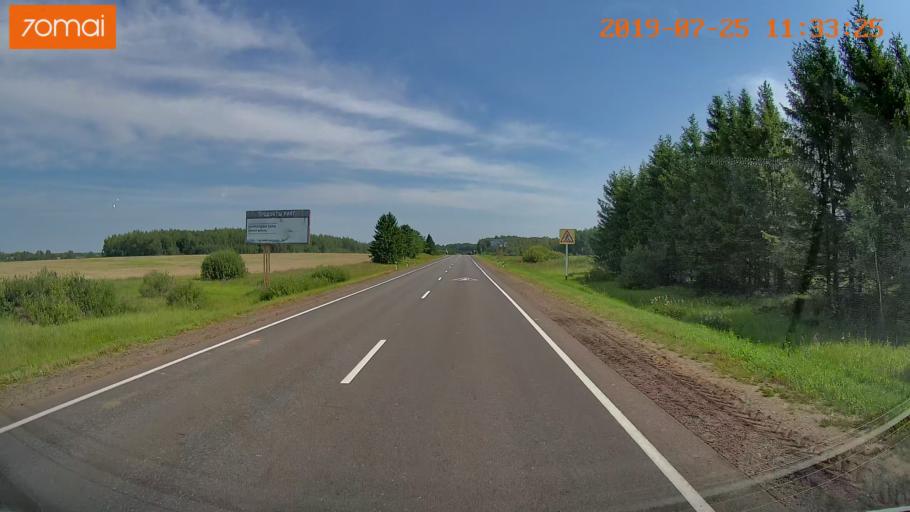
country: RU
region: Ivanovo
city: Privolzhsk
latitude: 57.3937
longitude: 41.3906
